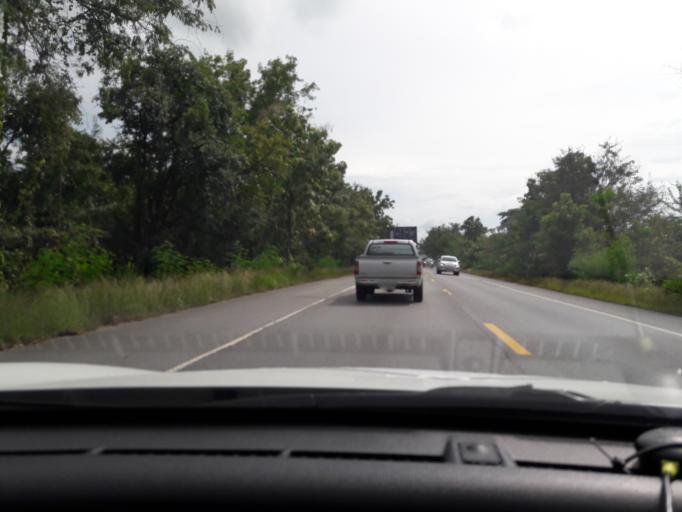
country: TH
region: Nakhon Sawan
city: Phai Sali
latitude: 15.5518
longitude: 100.5554
